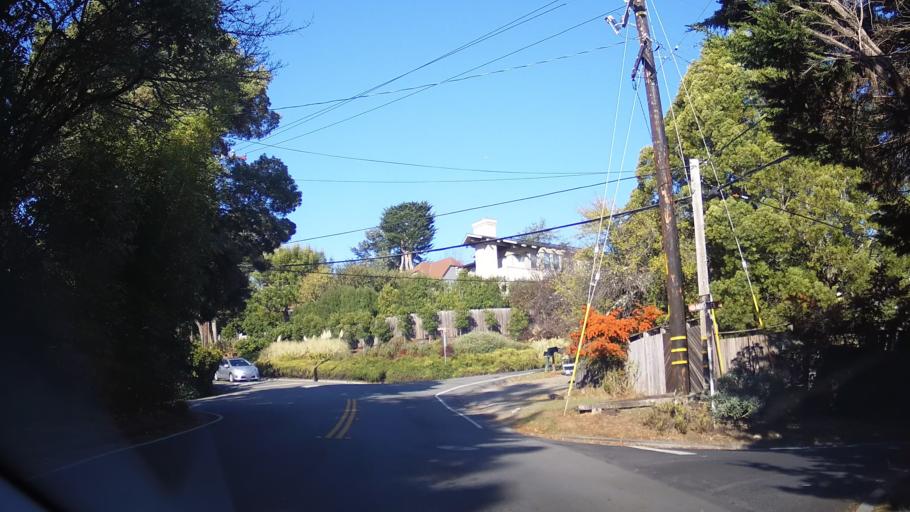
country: US
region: California
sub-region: Marin County
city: Mill Valley
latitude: 37.9001
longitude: -122.5447
